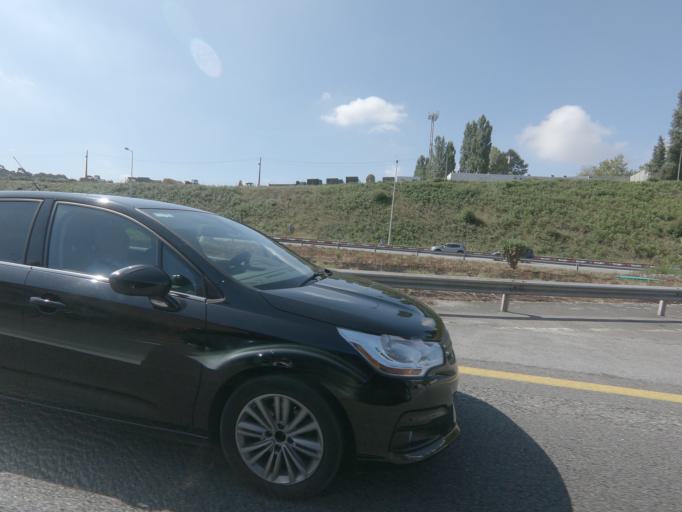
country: PT
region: Porto
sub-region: Maia
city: Pedroucos
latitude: 41.1989
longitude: -8.5738
